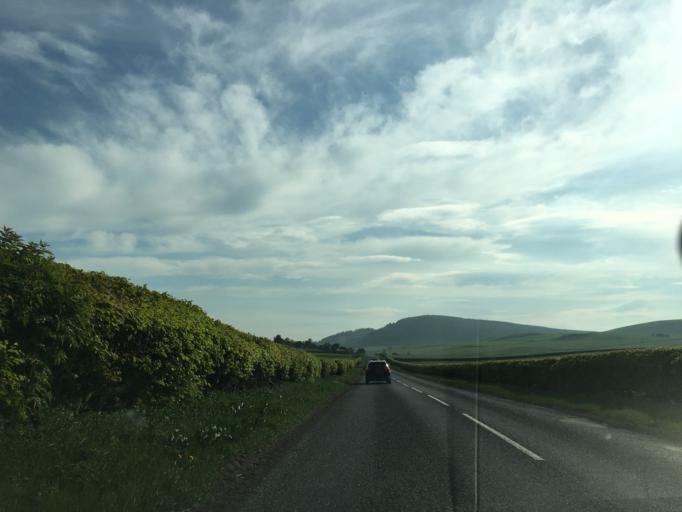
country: GB
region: Scotland
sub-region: The Scottish Borders
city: West Linton
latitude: 55.6784
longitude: -3.4044
